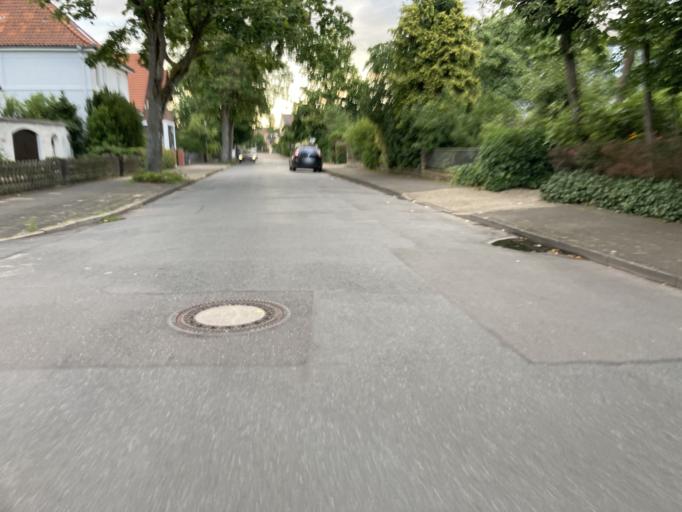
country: DE
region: Lower Saxony
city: Verden
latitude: 52.9165
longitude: 9.2363
